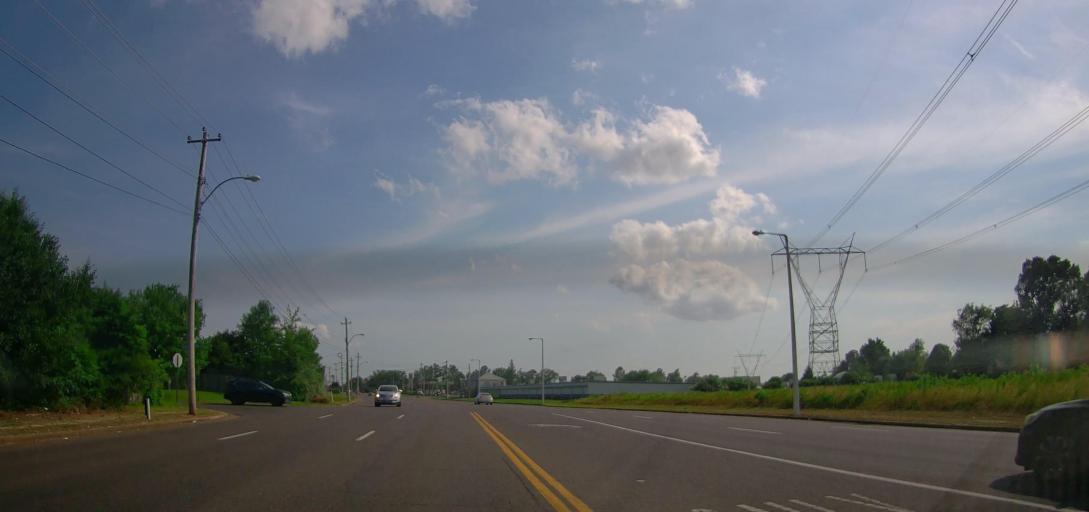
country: US
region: Mississippi
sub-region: De Soto County
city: Olive Branch
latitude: 35.0234
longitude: -89.8483
